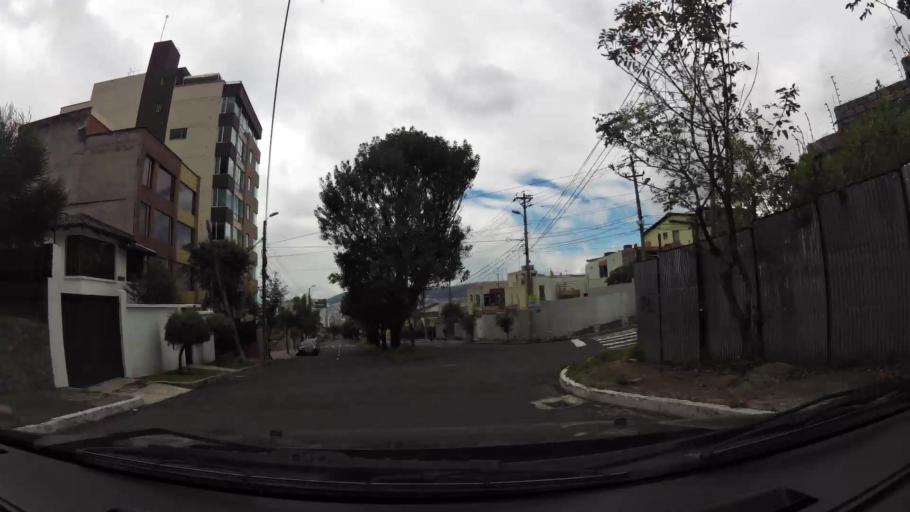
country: EC
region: Pichincha
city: Quito
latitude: -0.1713
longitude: -78.4991
